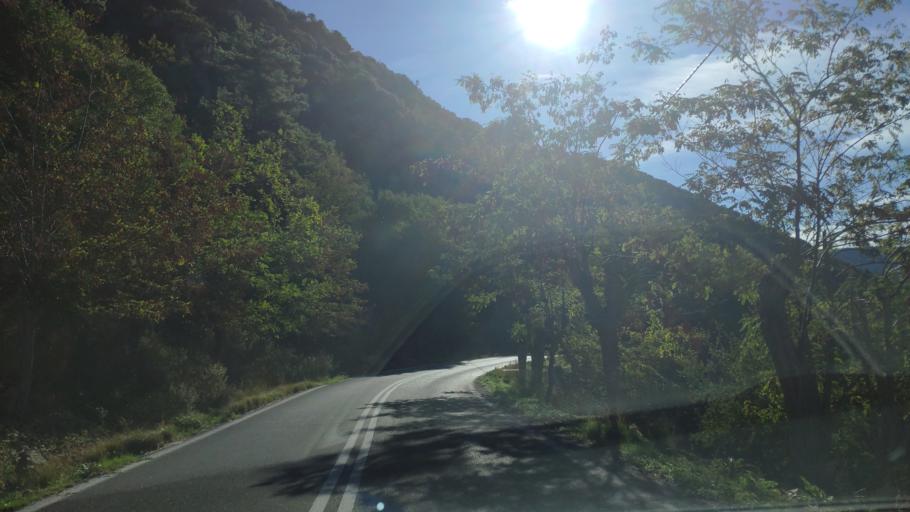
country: GR
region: Peloponnese
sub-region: Nomos Arkadias
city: Dimitsana
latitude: 37.5880
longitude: 22.0459
